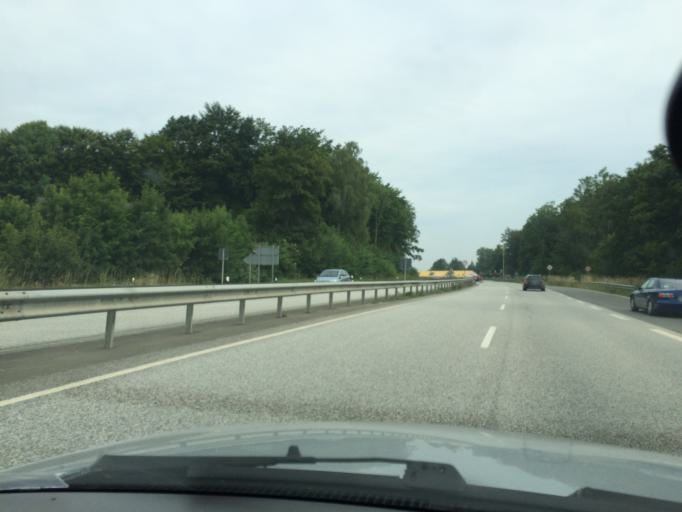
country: DK
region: South Denmark
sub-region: Aabenraa Kommune
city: Krusa
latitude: 54.8318
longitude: 9.4140
